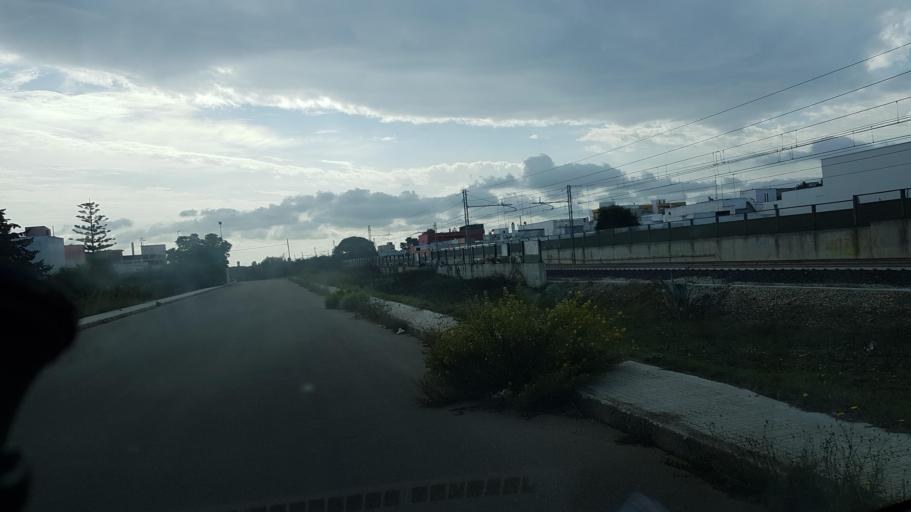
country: IT
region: Apulia
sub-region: Provincia di Brindisi
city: San Pietro Vernotico
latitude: 40.4820
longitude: 18.0060
